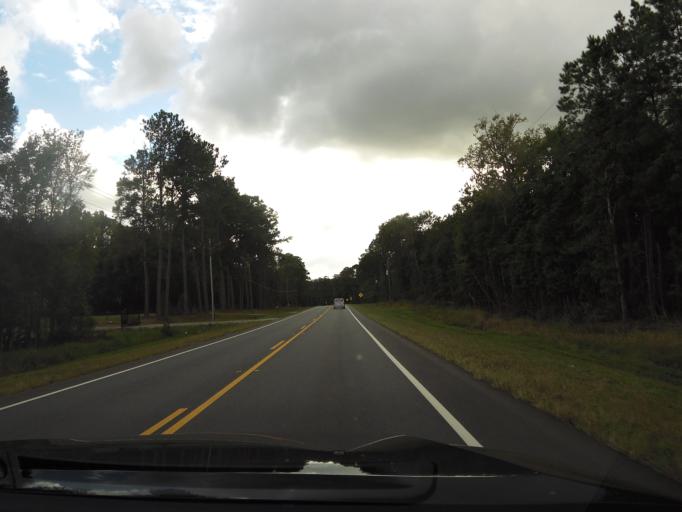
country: US
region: Georgia
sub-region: Liberty County
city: Midway
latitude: 31.8298
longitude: -81.4261
